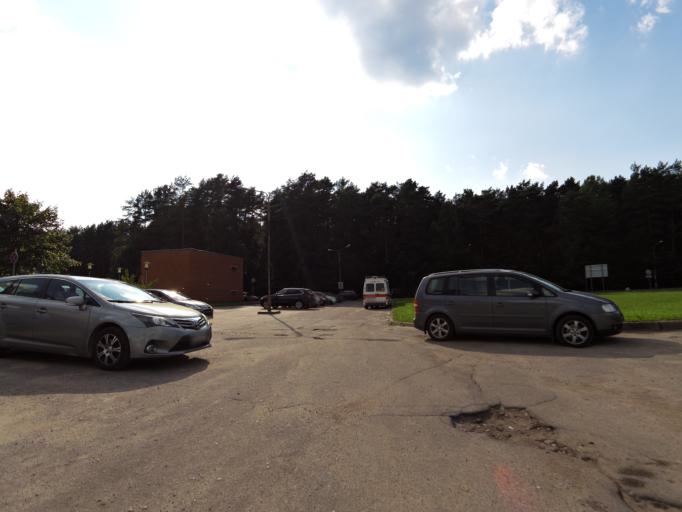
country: LT
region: Vilnius County
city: Lazdynai
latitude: 54.6687
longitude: 25.2066
